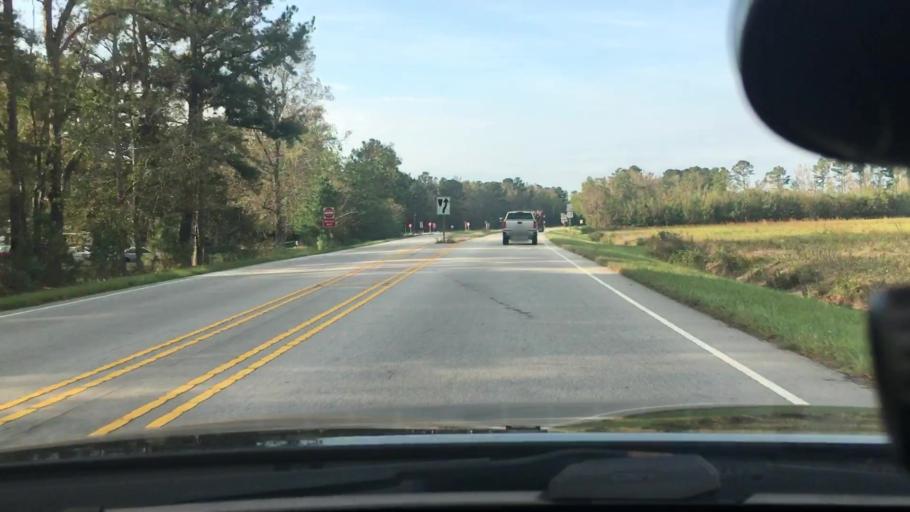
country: US
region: North Carolina
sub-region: Craven County
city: Vanceboro
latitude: 35.3313
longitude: -77.1500
